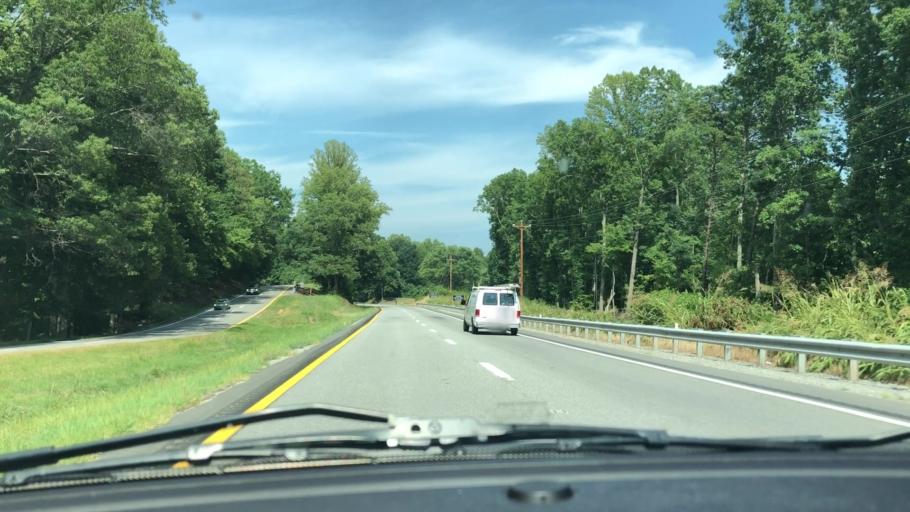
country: US
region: North Carolina
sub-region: Rockingham County
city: Stoneville
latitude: 36.5461
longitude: -79.9029
